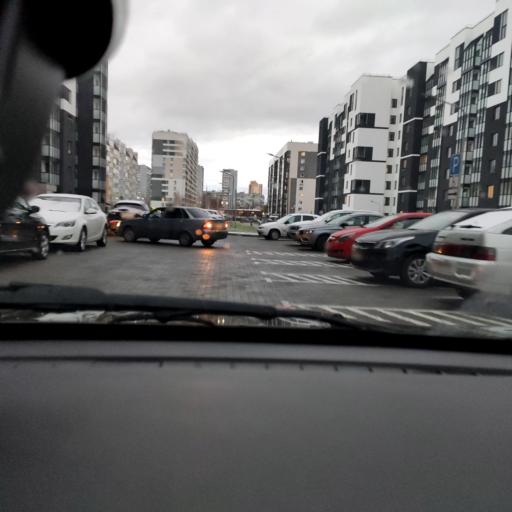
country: RU
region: Samara
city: Tol'yatti
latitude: 53.5268
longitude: 49.3403
